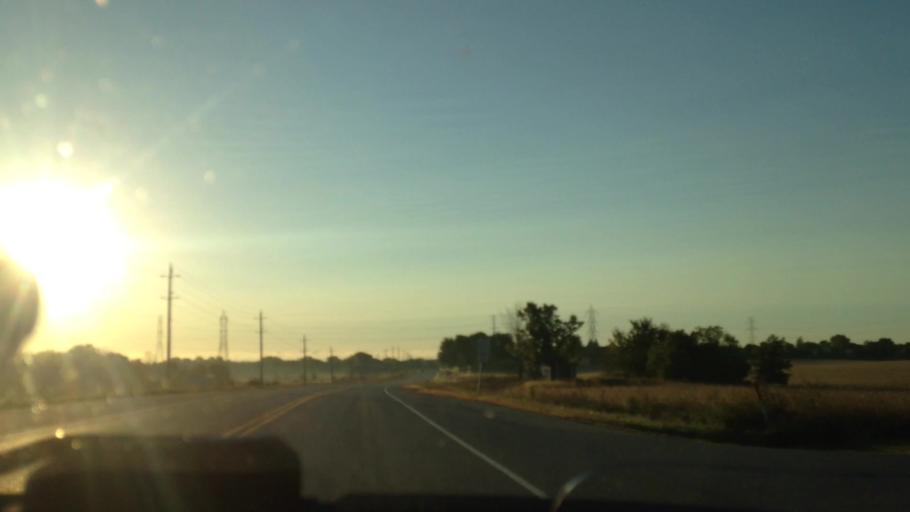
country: US
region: Wisconsin
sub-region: Ozaukee County
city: Saukville
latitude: 43.3882
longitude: -87.9641
